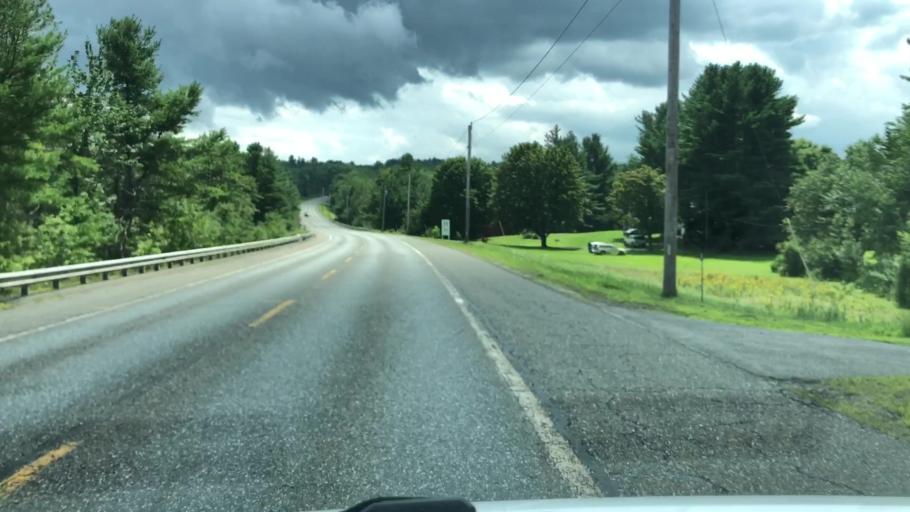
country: US
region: Massachusetts
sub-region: Franklin County
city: Ashfield
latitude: 42.4694
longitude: -72.8094
